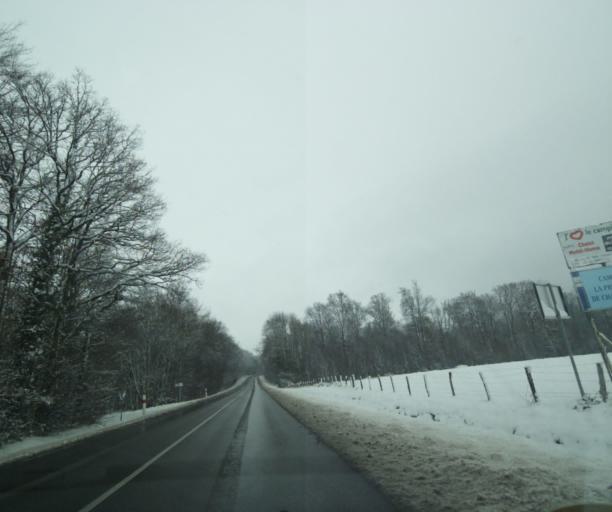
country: FR
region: Champagne-Ardenne
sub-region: Departement de la Haute-Marne
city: Montier-en-Der
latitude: 48.4875
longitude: 4.7755
